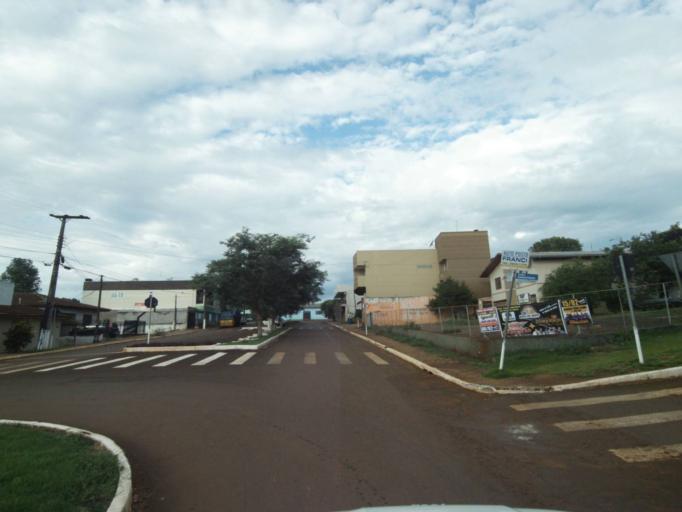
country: BR
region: Parana
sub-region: Laranjeiras Do Sul
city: Laranjeiras do Sul
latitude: -25.4899
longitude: -52.5260
